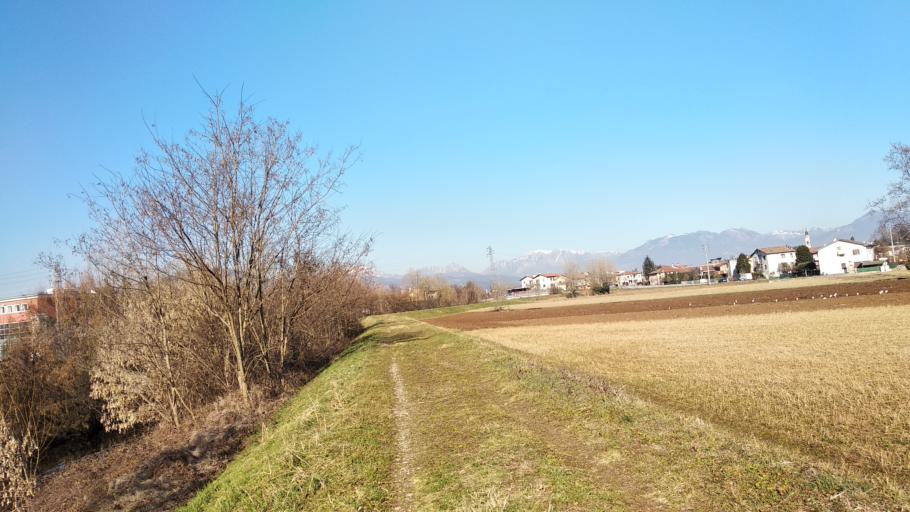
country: IT
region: Veneto
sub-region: Provincia di Vicenza
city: Motta
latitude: 45.5926
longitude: 11.5001
